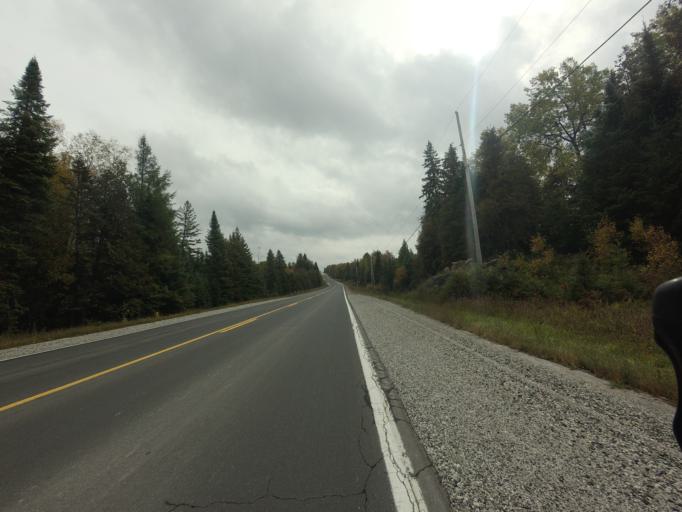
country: CA
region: Ontario
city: Perth
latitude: 45.1050
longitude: -76.4748
